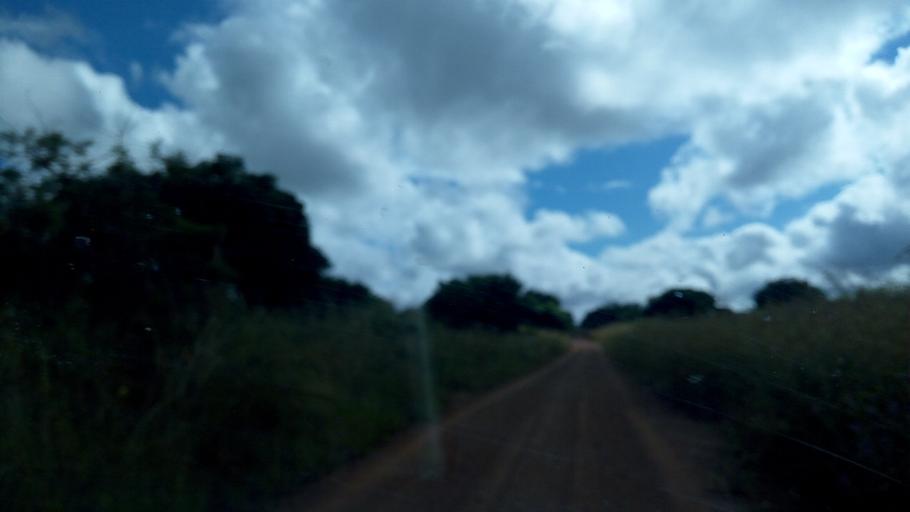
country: ZM
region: Northern
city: Kaputa
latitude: -8.4232
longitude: 28.9279
